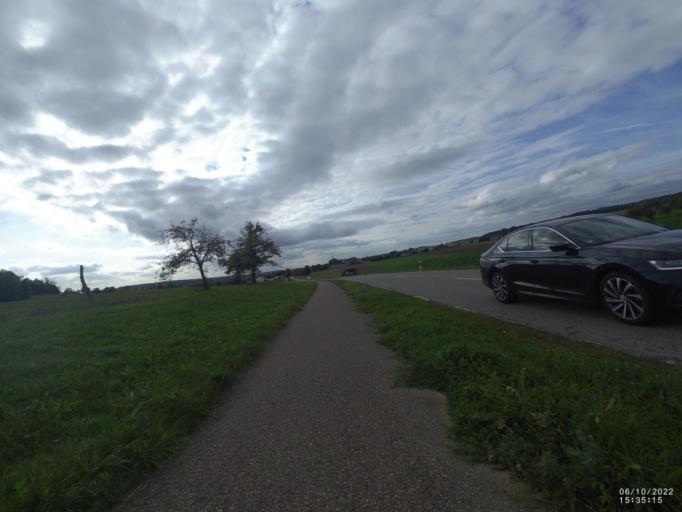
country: DE
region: Baden-Wuerttemberg
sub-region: Regierungsbezirk Stuttgart
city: Wangen
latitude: 48.7231
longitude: 9.5969
